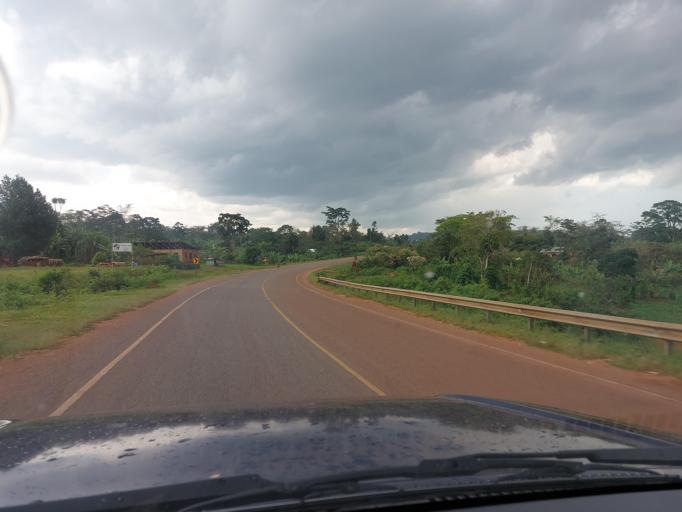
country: UG
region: Central Region
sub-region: Mukono District
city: Mukono
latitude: 0.2646
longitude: 32.8392
